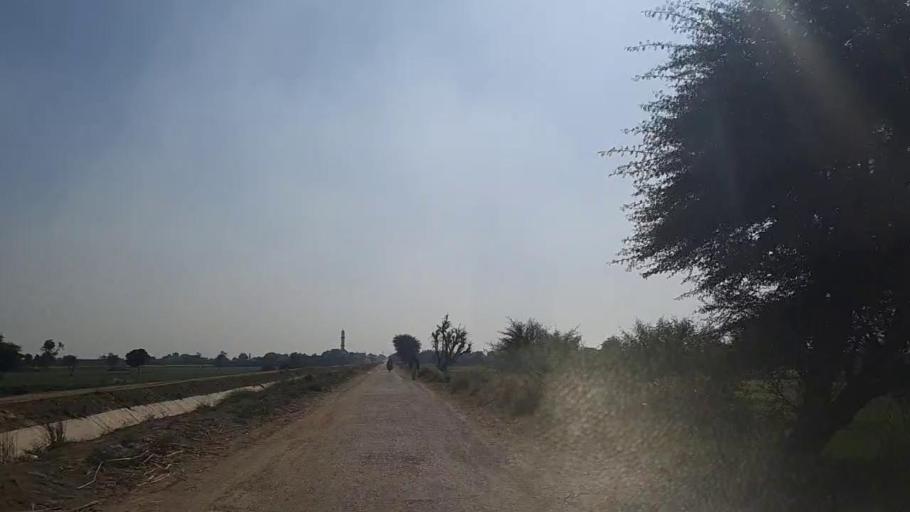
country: PK
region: Sindh
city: Shahpur Chakar
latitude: 26.1935
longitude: 68.5836
